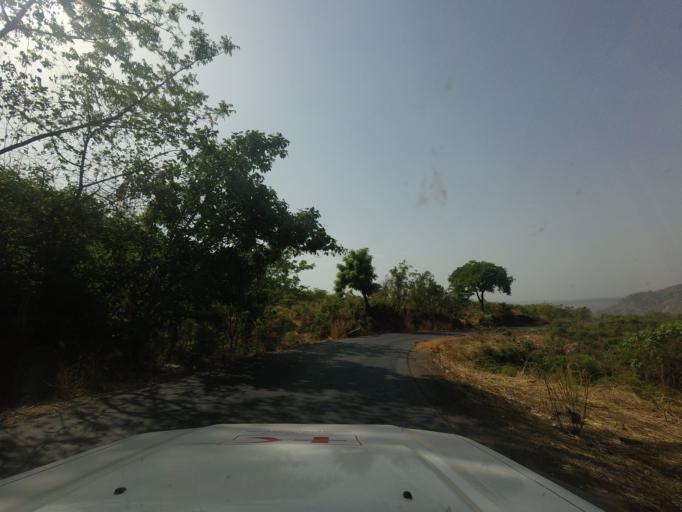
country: GN
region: Mamou
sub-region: Mamou Prefecture
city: Mamou
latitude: 10.2229
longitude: -12.4609
